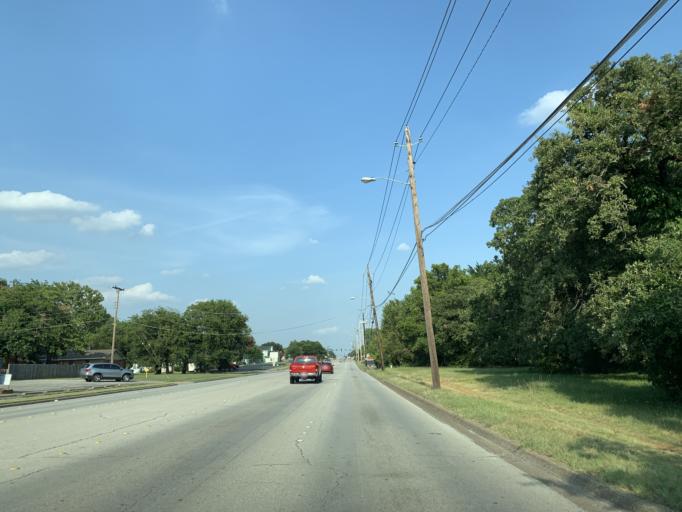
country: US
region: Texas
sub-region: Tarrant County
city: Hurst
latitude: 32.8236
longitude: -97.1950
